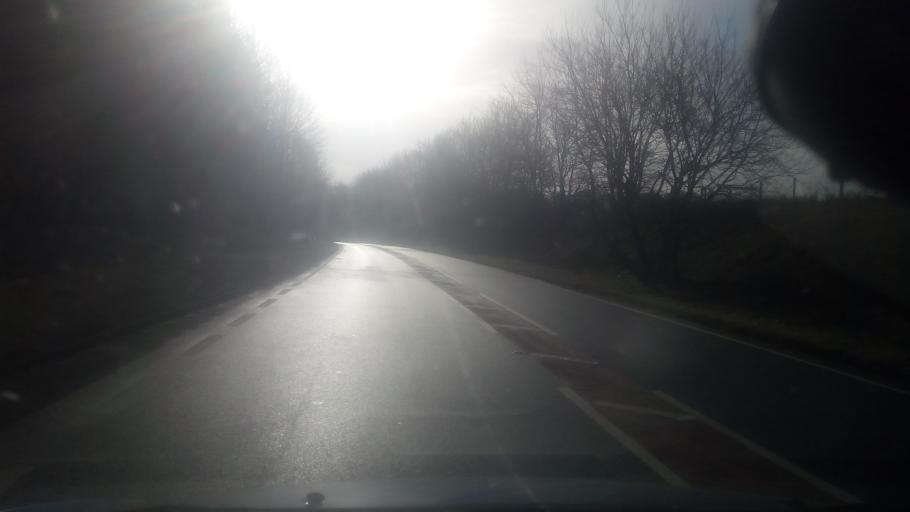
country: GB
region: Scotland
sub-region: The Scottish Borders
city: Jedburgh
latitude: 55.4368
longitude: -2.5426
